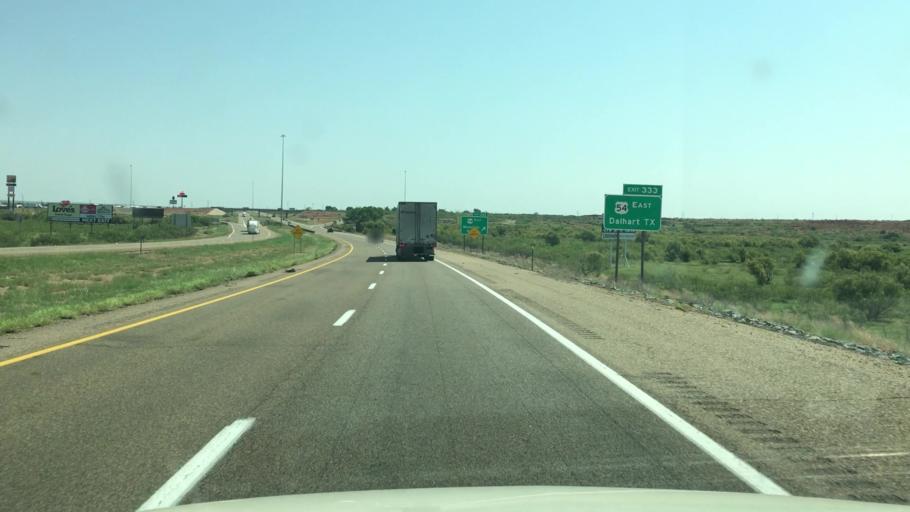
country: US
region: New Mexico
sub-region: Quay County
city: Tucumcari
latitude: 35.1522
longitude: -103.7113
